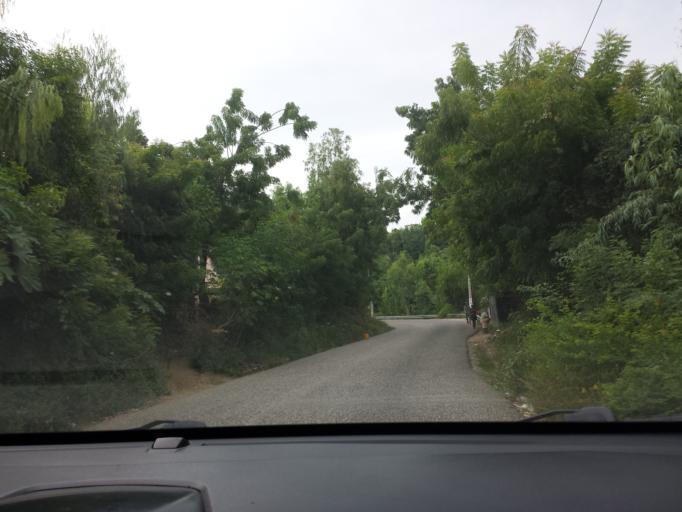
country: HT
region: Ouest
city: Leogane
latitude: 18.4337
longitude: -72.6430
